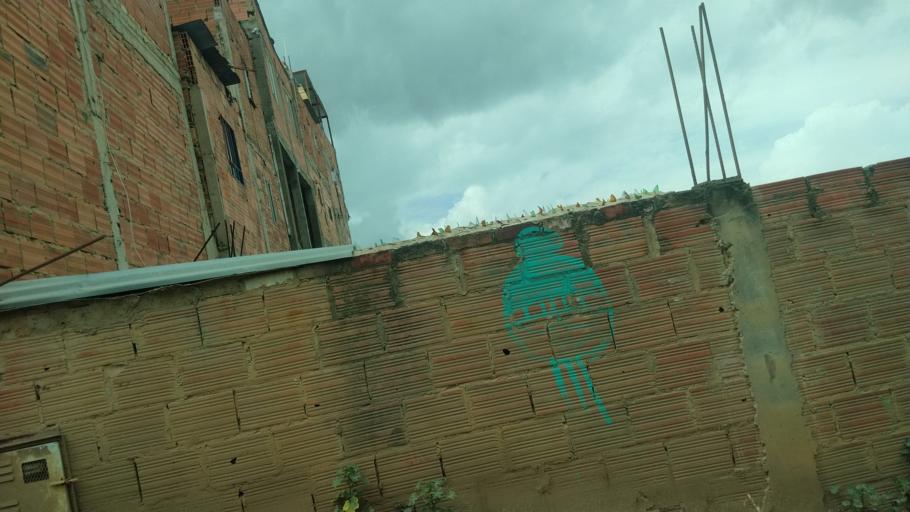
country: CO
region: Cundinamarca
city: Soacha
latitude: 4.5810
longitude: -74.1836
